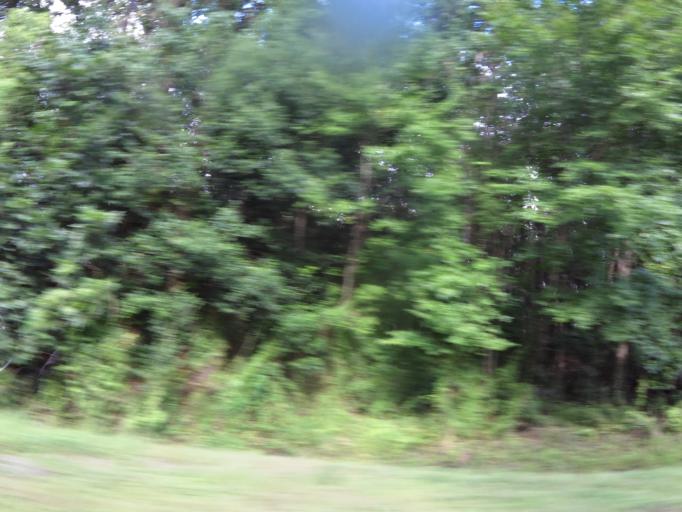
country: US
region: Florida
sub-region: Duval County
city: Jacksonville
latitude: 30.3302
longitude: -81.7435
